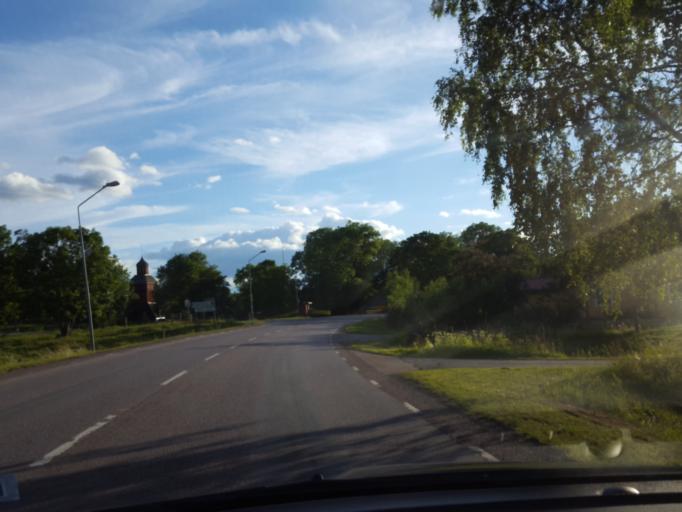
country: SE
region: Uppsala
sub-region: Osthammars Kommun
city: Gimo
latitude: 60.2168
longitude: 18.2111
